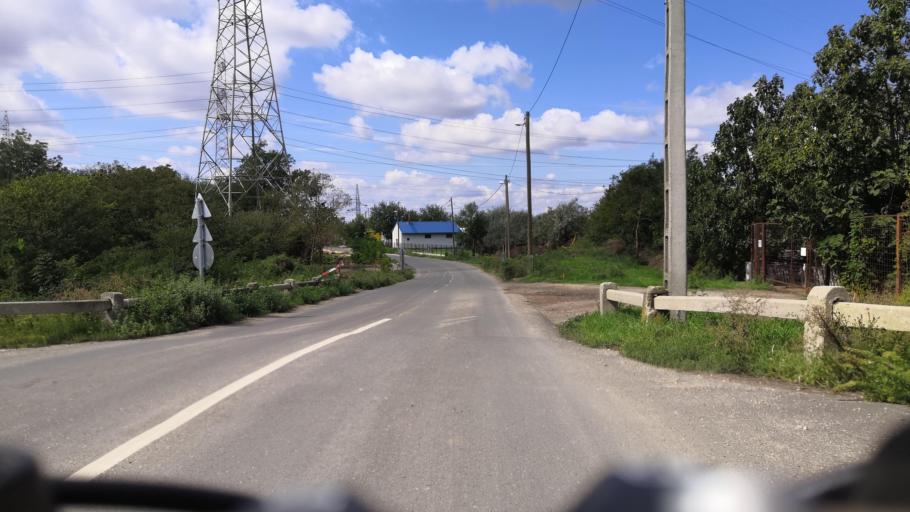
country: HU
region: Csongrad
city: Szeged
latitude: 46.2775
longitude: 20.1363
